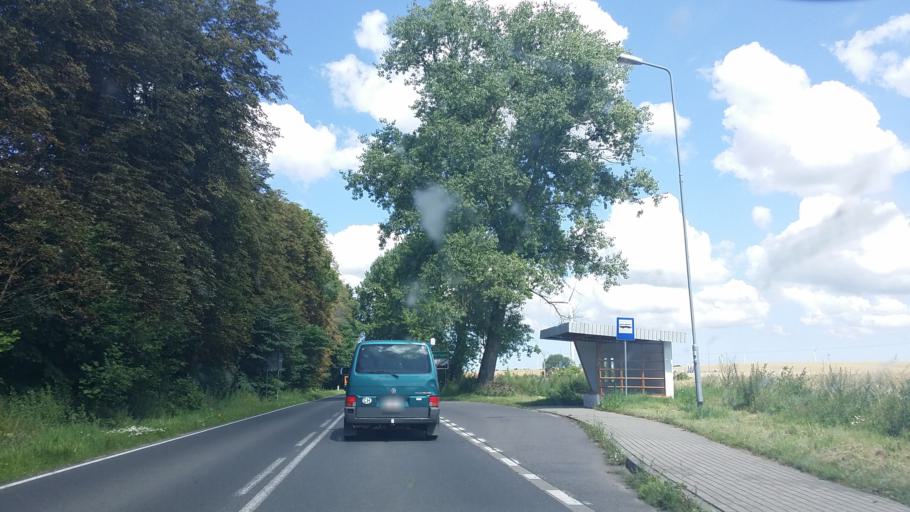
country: PL
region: West Pomeranian Voivodeship
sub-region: Powiat kolobrzeski
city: Goscino
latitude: 54.0020
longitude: 15.6744
